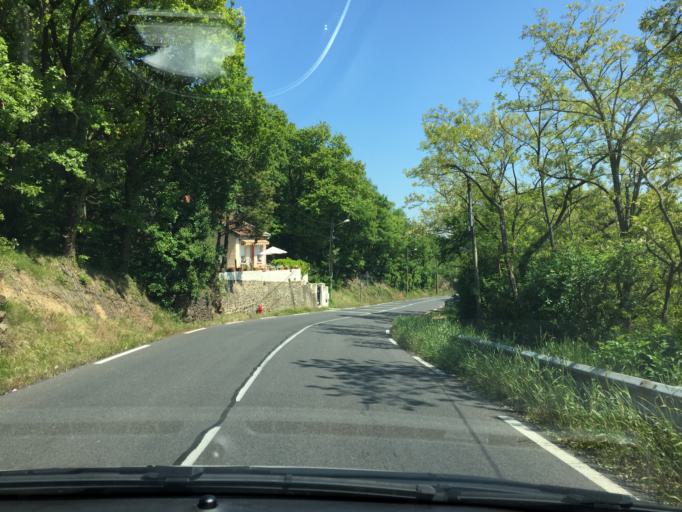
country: FR
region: Rhone-Alpes
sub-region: Departement du Rhone
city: Chassagny
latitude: 45.5848
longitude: 4.7391
